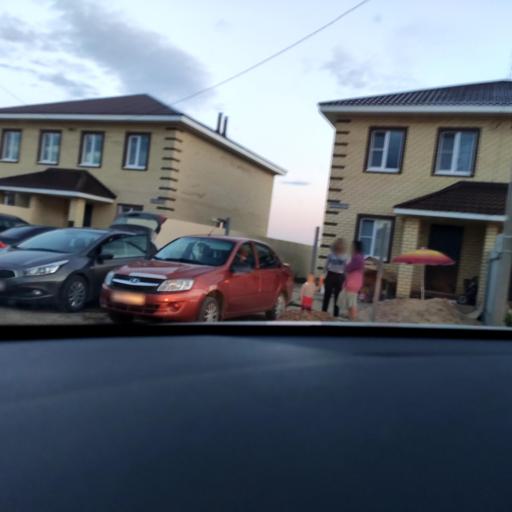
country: RU
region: Tatarstan
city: Stolbishchi
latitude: 55.7175
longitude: 49.2966
